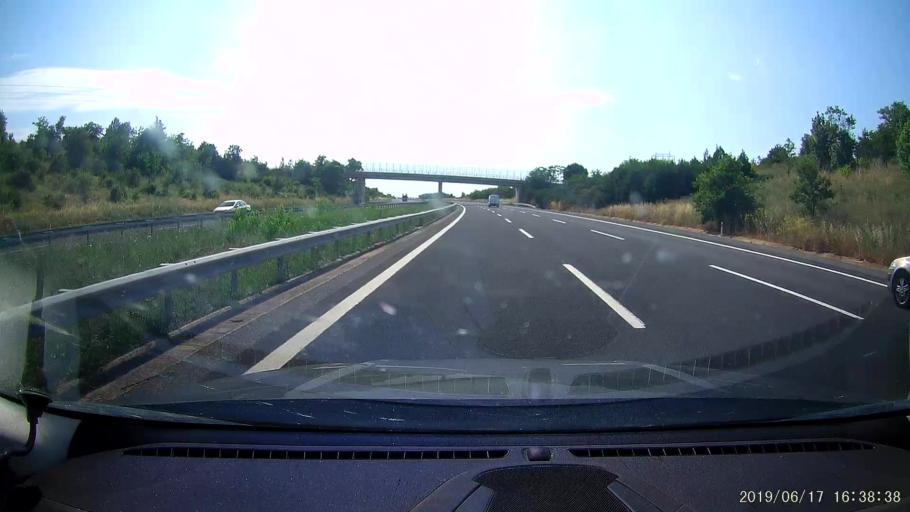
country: TR
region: Kirklareli
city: Luleburgaz
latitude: 41.4471
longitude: 27.4368
